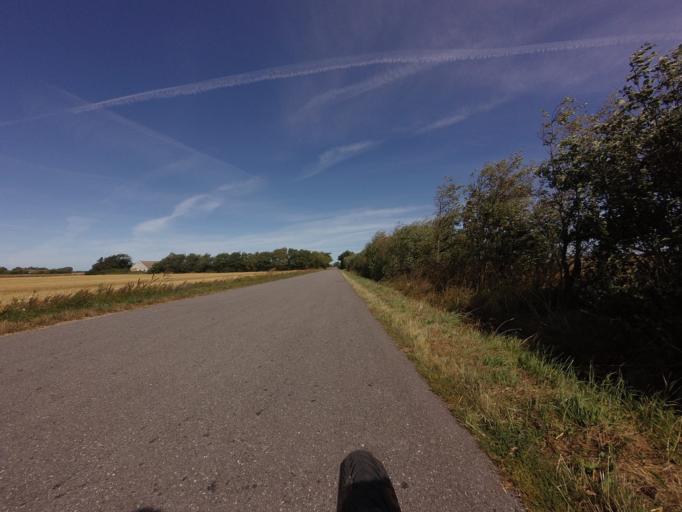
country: DK
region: North Denmark
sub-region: Bronderslev Kommune
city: Bronderslev
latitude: 57.3184
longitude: 9.8148
